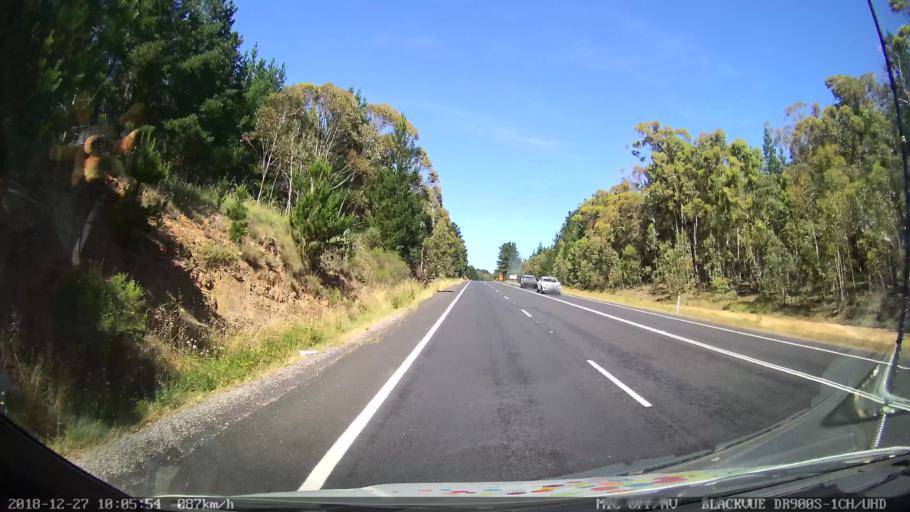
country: AU
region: New South Wales
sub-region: Lithgow
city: Portland
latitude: -33.4357
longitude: 149.8641
